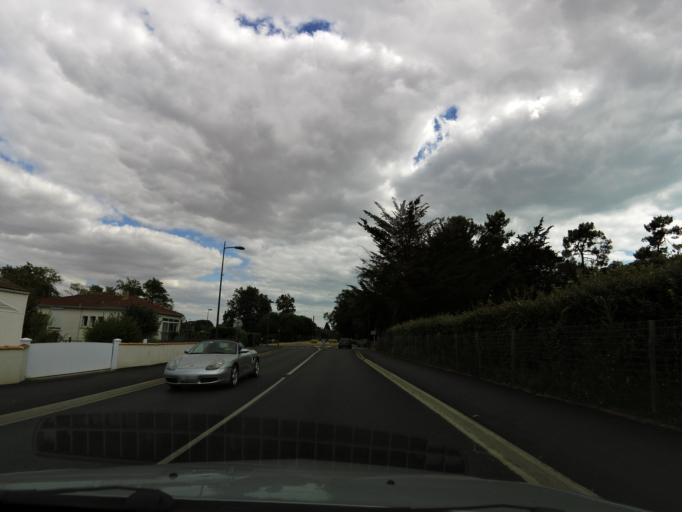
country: FR
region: Pays de la Loire
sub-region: Departement de la Vendee
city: Longeville-sur-Mer
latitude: 46.4093
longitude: -1.4938
